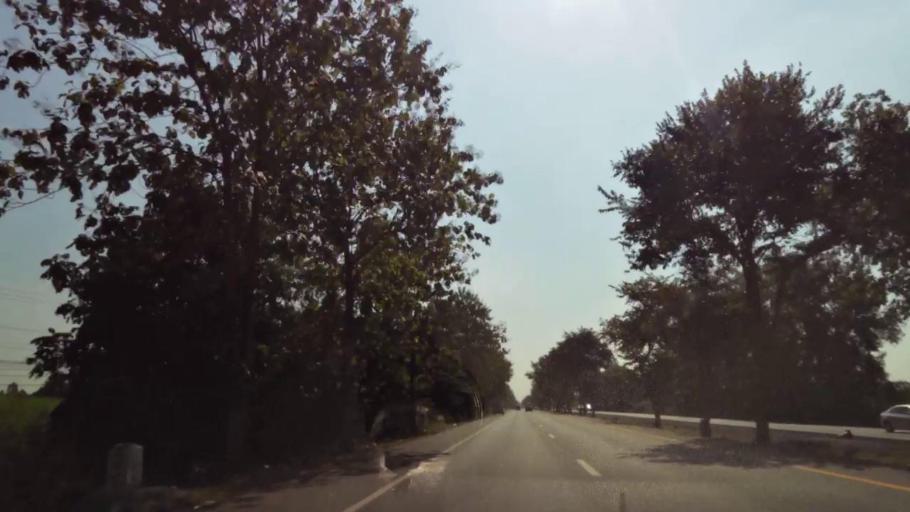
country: TH
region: Phichit
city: Bueng Na Rang
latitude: 16.0812
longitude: 100.1246
